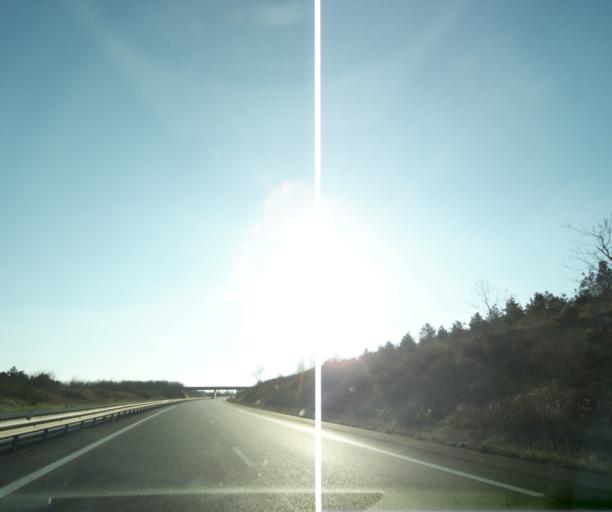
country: FR
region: Midi-Pyrenees
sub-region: Departement du Tarn-et-Garonne
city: Albias
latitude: 44.0604
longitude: 1.4218
